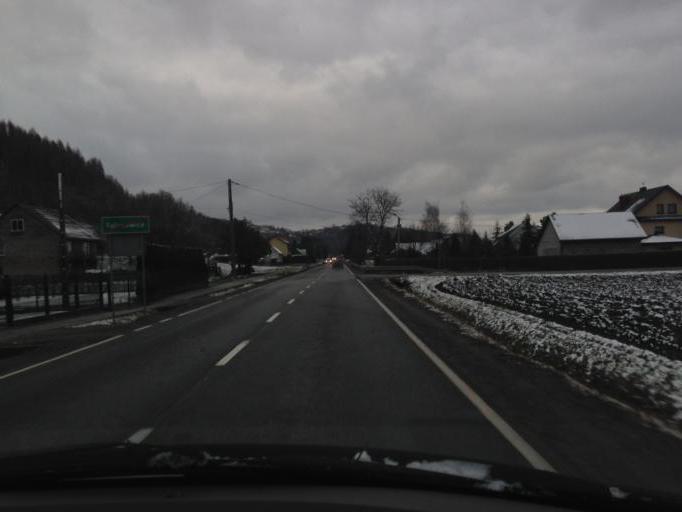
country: PL
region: Lesser Poland Voivodeship
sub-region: Powiat brzeski
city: Zlota
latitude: 49.8661
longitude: 20.7428
